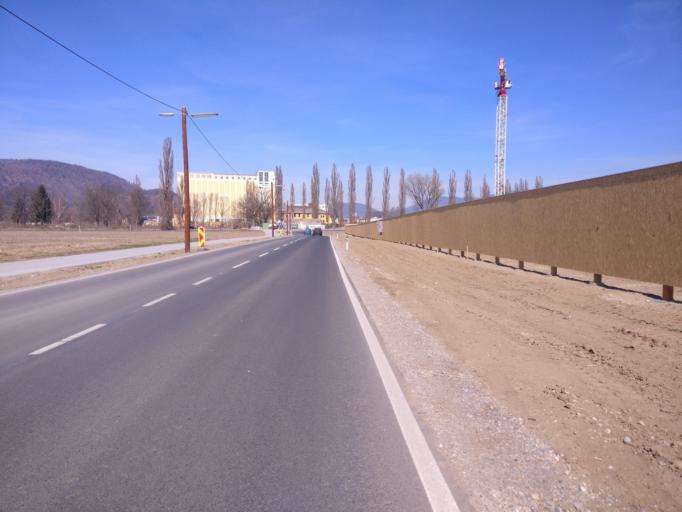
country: AT
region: Styria
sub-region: Graz Stadt
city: Wetzelsdorf
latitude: 47.0593
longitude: 15.4103
